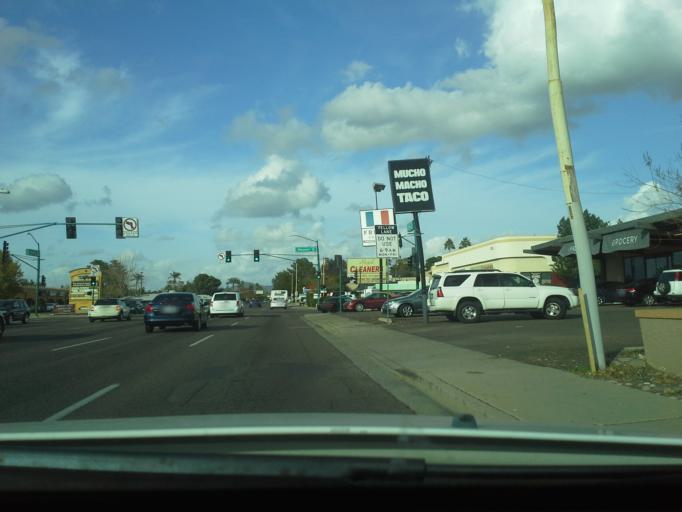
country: US
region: Arizona
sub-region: Maricopa County
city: Phoenix
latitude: 33.5160
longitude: -112.0823
